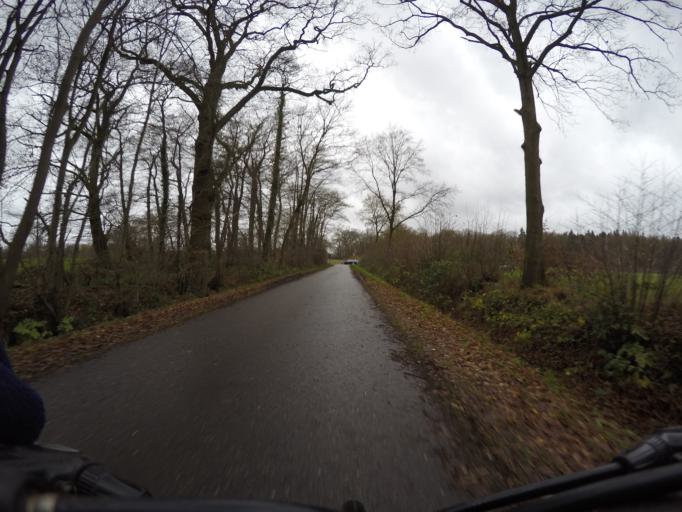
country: DE
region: Schleswig-Holstein
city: Quickborn
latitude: 53.7154
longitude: 9.8869
